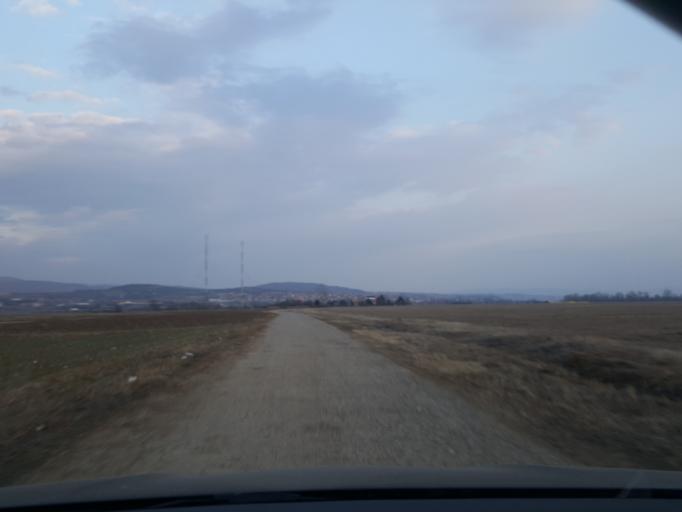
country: RS
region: Central Serbia
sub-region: Nisavski Okrug
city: Aleksinac
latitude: 43.5532
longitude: 21.6603
